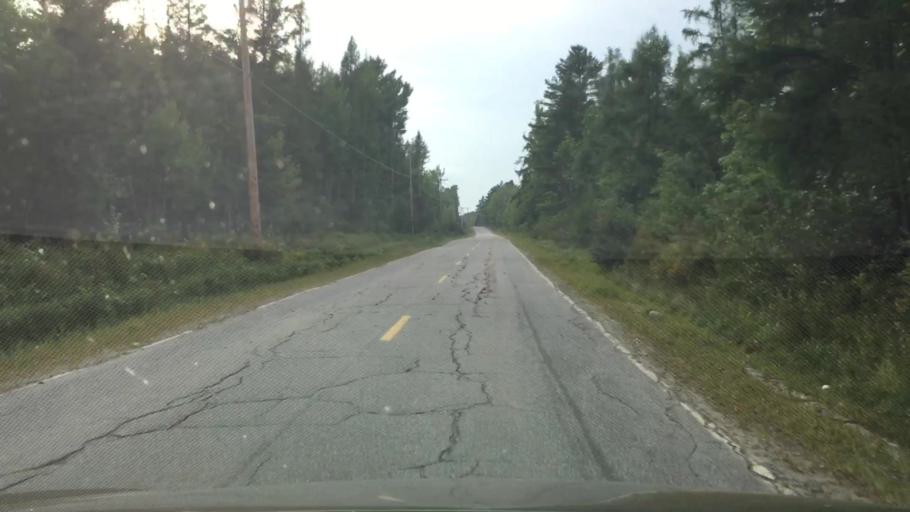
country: US
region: Maine
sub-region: Hancock County
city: Penobscot
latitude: 44.4711
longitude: -68.7494
